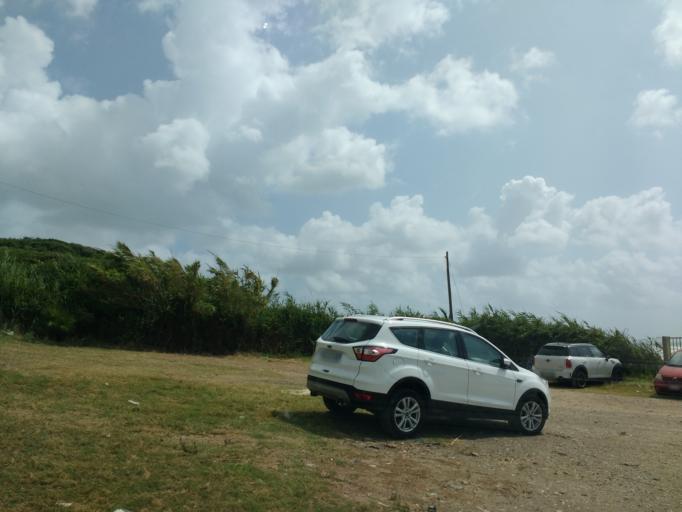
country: IT
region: Latium
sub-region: Citta metropolitana di Roma Capitale
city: Lavinio
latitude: 41.4899
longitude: 12.5890
